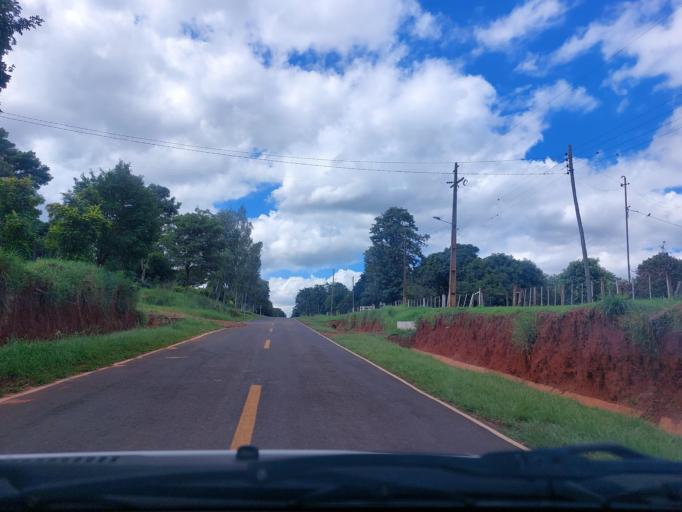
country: PY
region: San Pedro
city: Guayaybi
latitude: -24.5317
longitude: -56.5267
